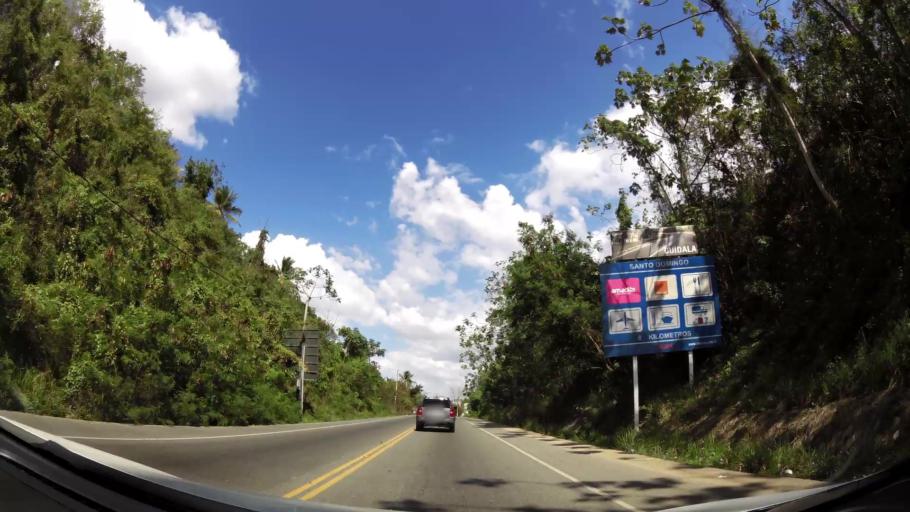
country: DO
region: San Cristobal
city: Bajos de Haina
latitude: 18.4278
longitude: -70.0514
